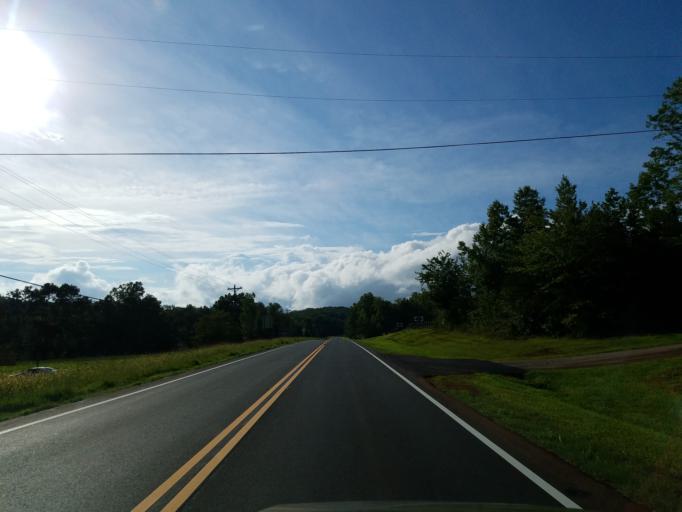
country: US
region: Georgia
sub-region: White County
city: Cleveland
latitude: 34.6360
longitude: -83.8285
